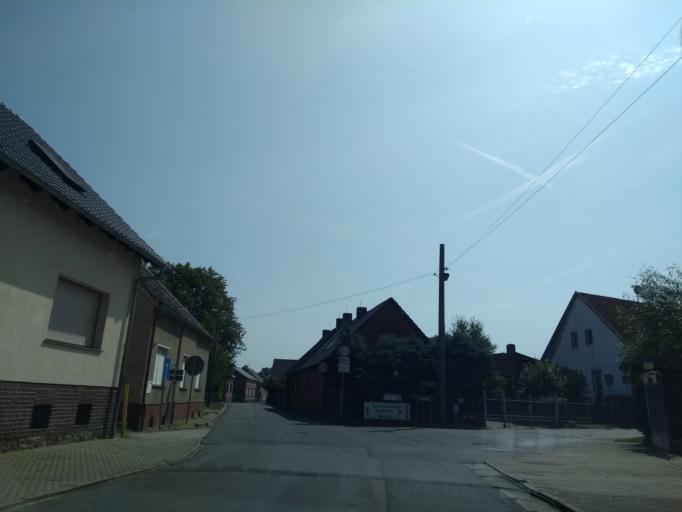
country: DE
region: Brandenburg
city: Vetschau
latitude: 51.8171
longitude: 14.0440
